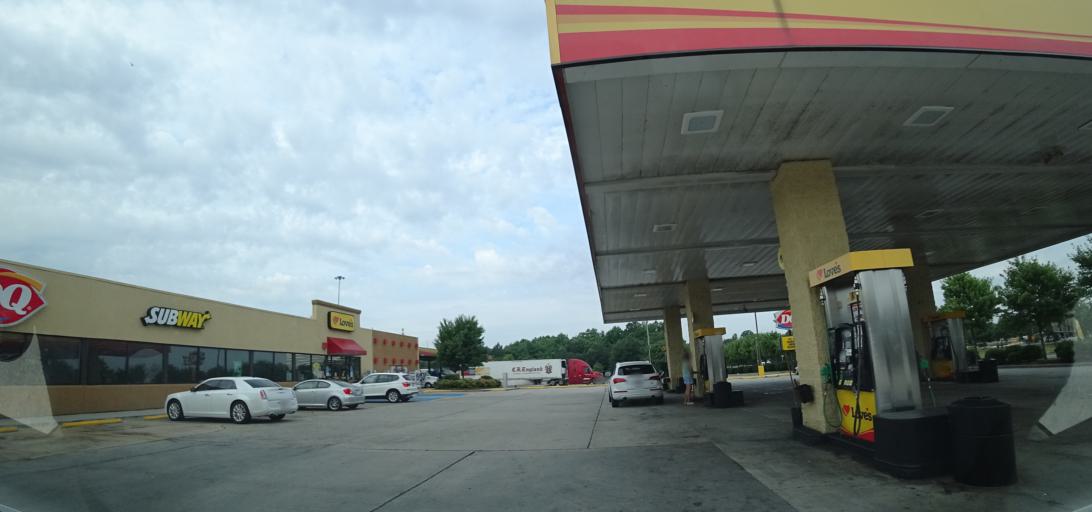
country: US
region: Virginia
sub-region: Caroline County
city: Bowling Green
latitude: 37.9383
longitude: -77.4657
